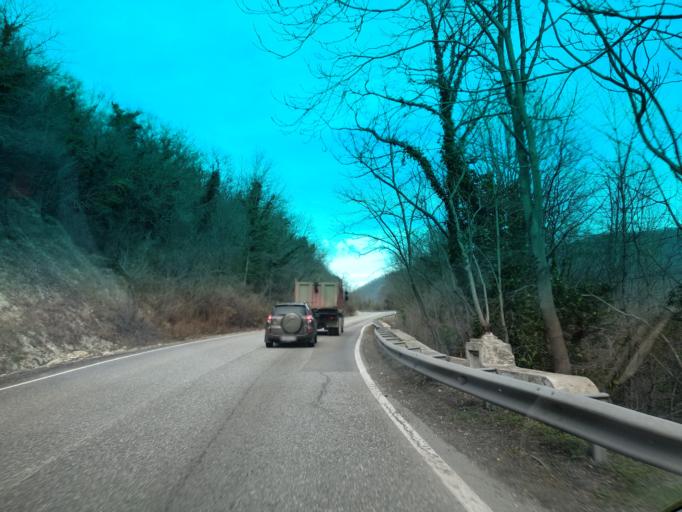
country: RU
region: Krasnodarskiy
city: Shepsi
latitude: 44.0605
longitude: 39.1338
